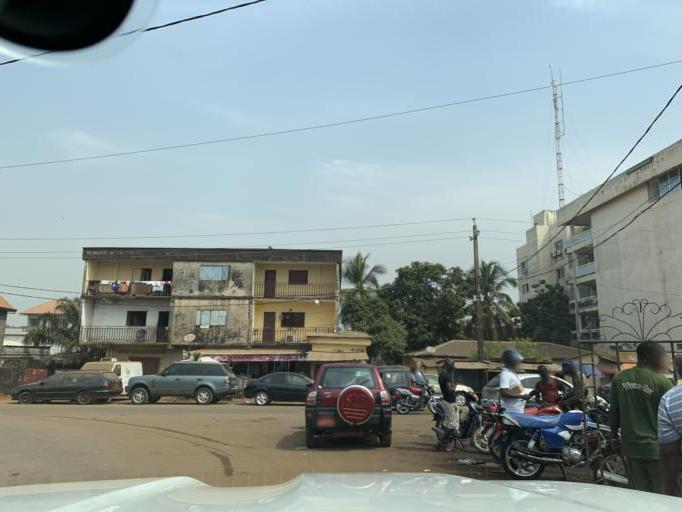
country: GN
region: Conakry
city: Conakry
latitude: 9.5535
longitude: -13.6681
